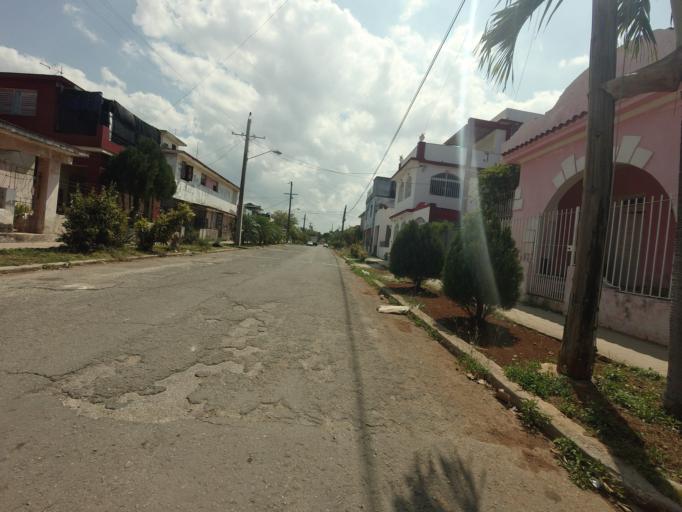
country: CU
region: La Habana
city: Cerro
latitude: 23.1093
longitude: -82.4255
